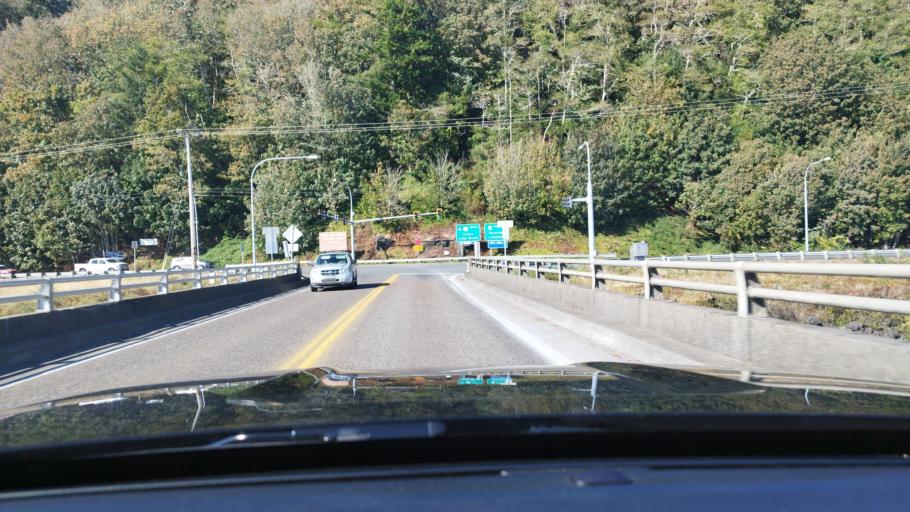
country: US
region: Oregon
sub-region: Clatsop County
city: Astoria
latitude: 46.2405
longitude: -123.8748
